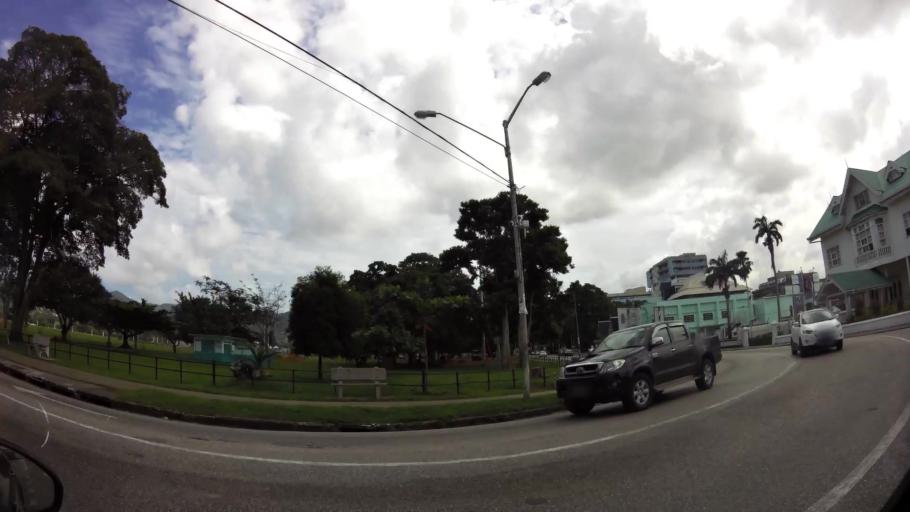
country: TT
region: City of Port of Spain
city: Port-of-Spain
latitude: 10.6645
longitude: -61.5165
